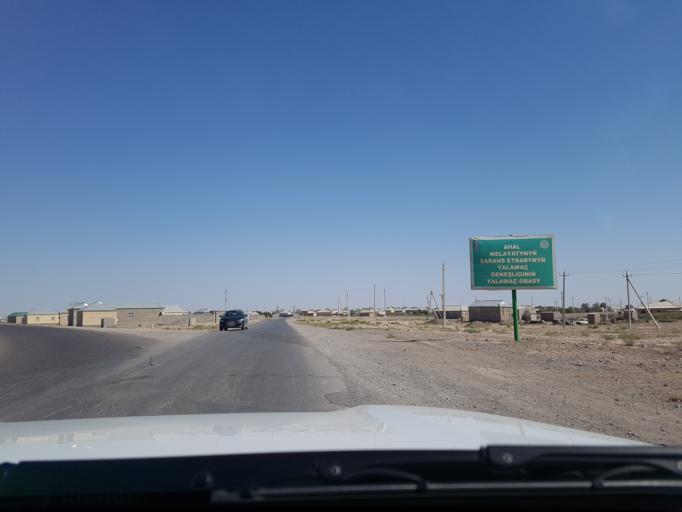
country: IR
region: Razavi Khorasan
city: Sarakhs
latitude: 36.5208
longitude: 61.2482
